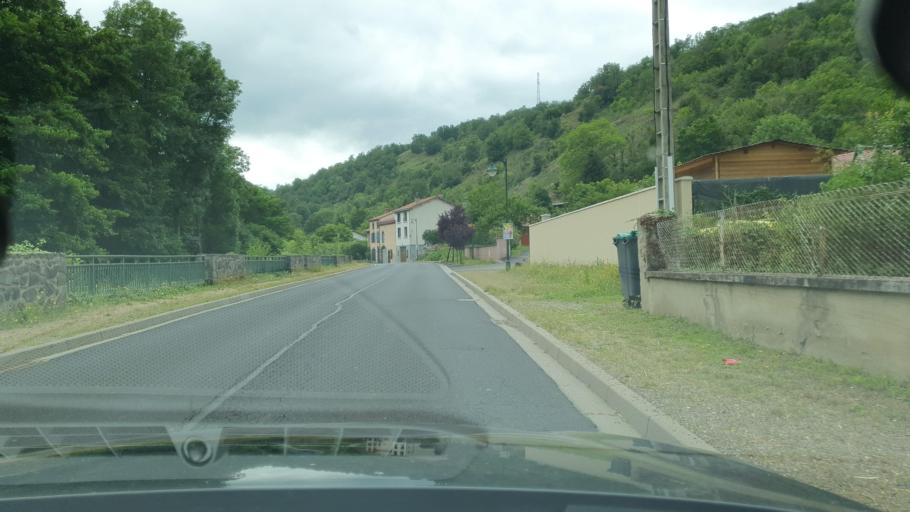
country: FR
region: Auvergne
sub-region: Departement du Puy-de-Dome
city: Champeix
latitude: 45.5837
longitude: 3.0878
